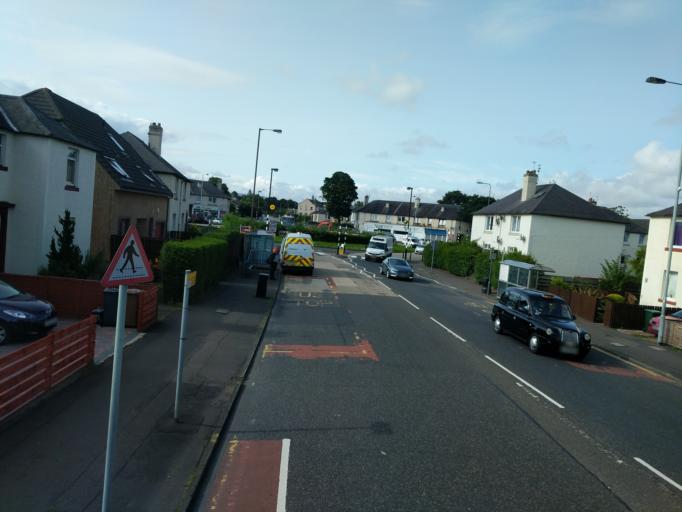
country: GB
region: Scotland
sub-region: Edinburgh
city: Colinton
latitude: 55.9331
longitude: -3.2589
